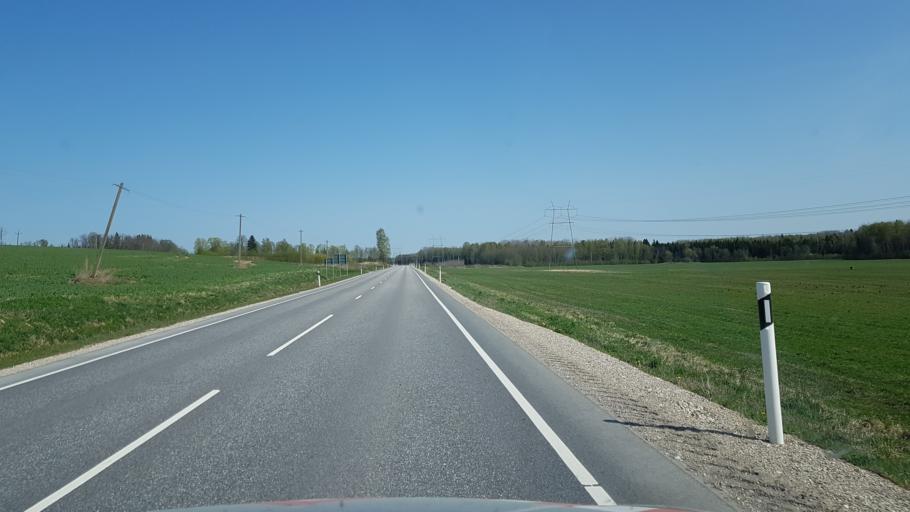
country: EE
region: Viljandimaa
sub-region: Abja vald
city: Abja-Paluoja
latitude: 58.2849
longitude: 25.2900
